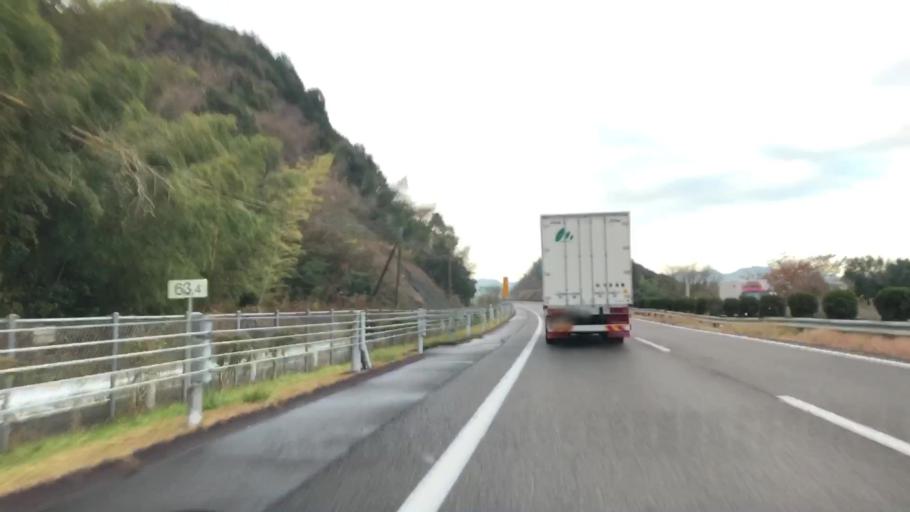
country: JP
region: Saga Prefecture
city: Ureshinomachi-shimojuku
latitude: 33.1538
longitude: 130.0024
